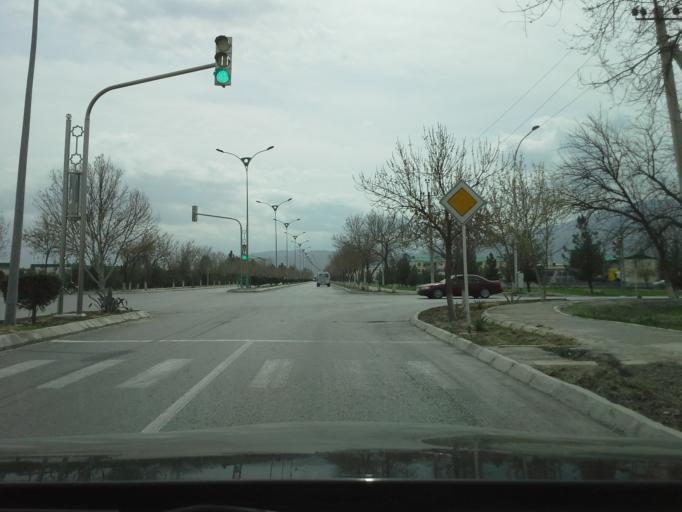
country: TM
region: Ahal
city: Abadan
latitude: 38.0604
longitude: 58.1589
